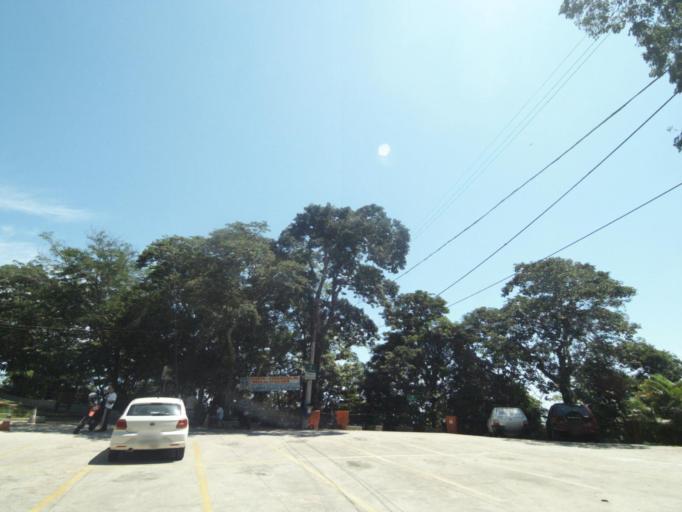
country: BR
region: Rio de Janeiro
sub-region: Niteroi
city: Niteroi
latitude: -22.9296
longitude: -43.0874
